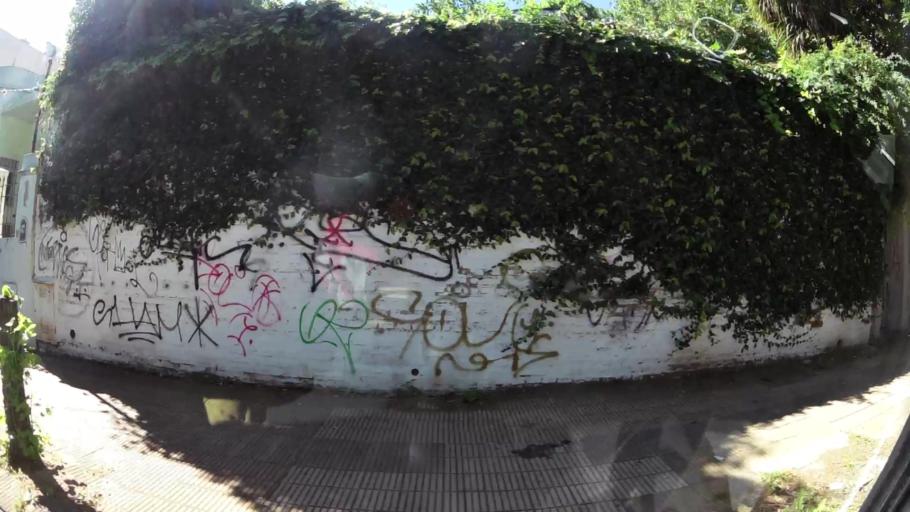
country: AR
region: Buenos Aires
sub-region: Partido de Vicente Lopez
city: Olivos
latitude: -34.5248
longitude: -58.4783
